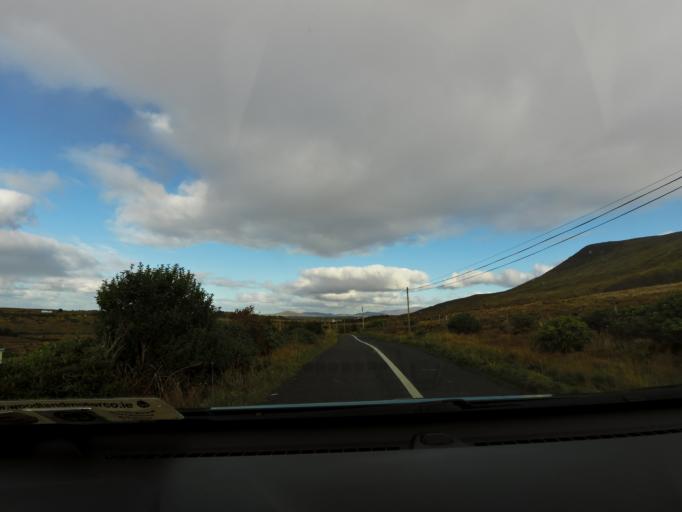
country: IE
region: Connaught
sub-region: Maigh Eo
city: Belmullet
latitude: 53.9339
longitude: -9.8946
